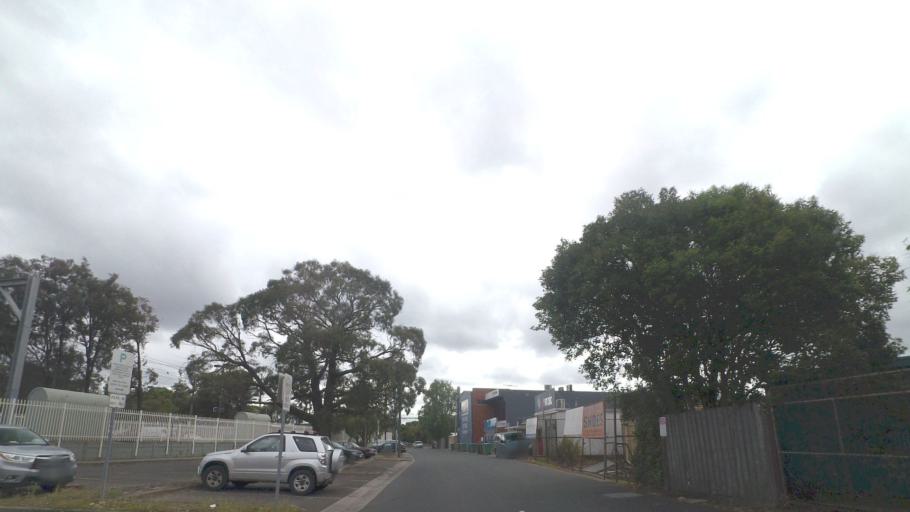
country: AU
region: Victoria
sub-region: Maroondah
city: Croydon South
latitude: -37.7956
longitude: 145.2808
